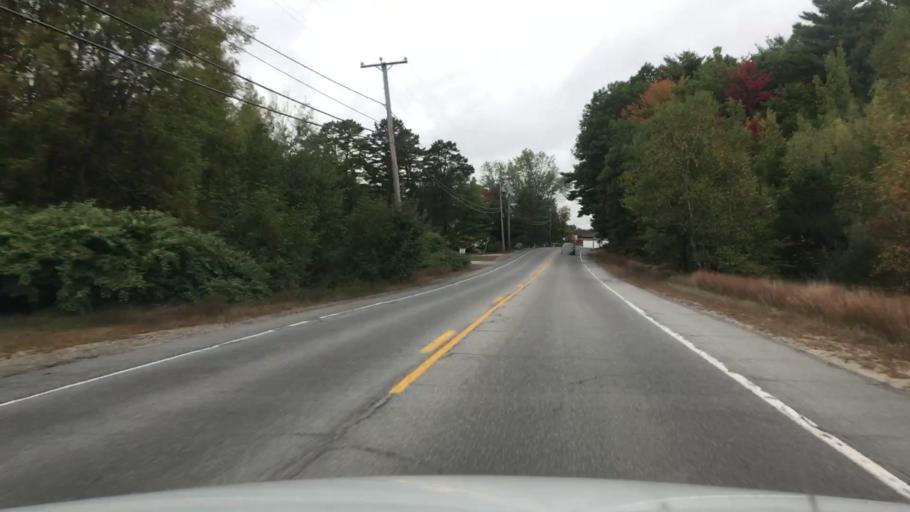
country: US
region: Maine
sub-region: Oxford County
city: Oxford
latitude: 44.1415
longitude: -70.4745
